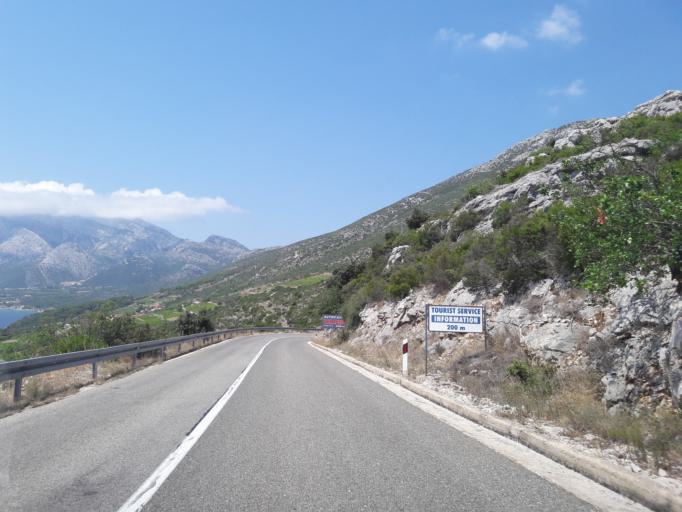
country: HR
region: Dubrovacko-Neretvanska
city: Orebic
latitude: 42.9718
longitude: 17.2413
